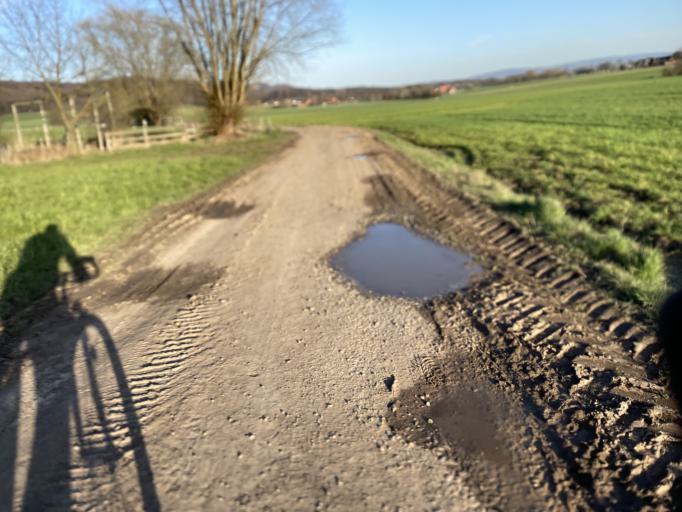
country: DE
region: North Rhine-Westphalia
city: Porta Westfalica
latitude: 52.2281
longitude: 8.9743
